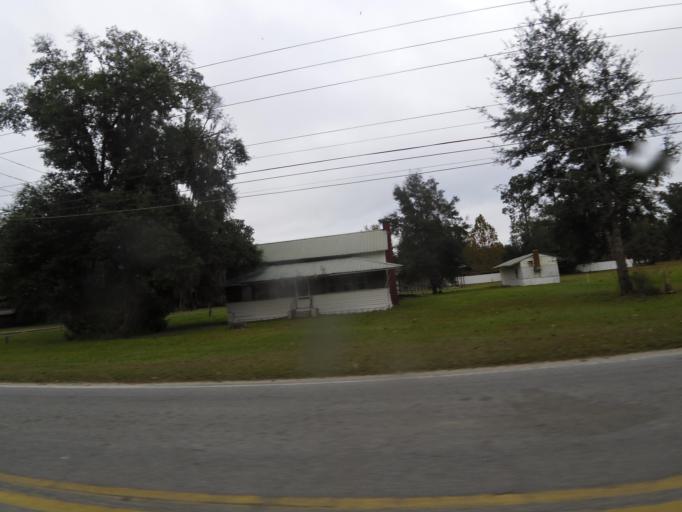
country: US
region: Georgia
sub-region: Charlton County
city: Folkston
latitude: 30.8319
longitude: -82.0103
